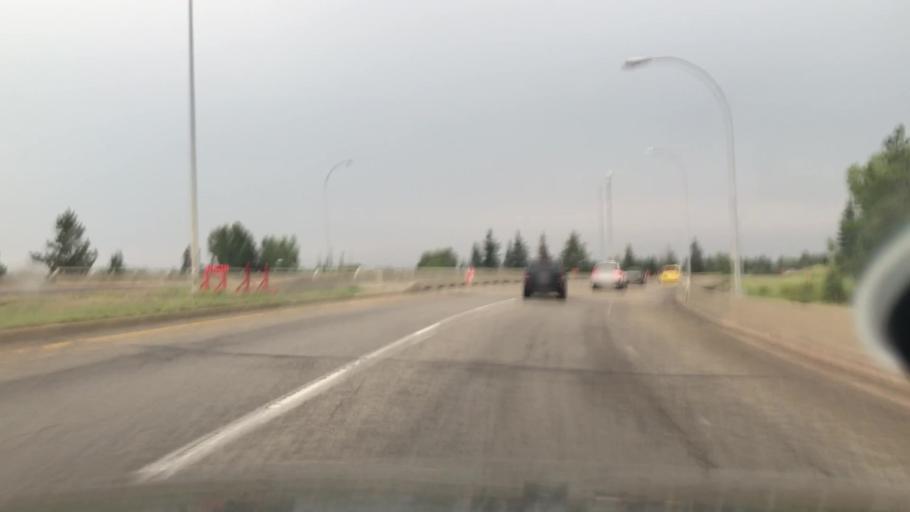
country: CA
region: Alberta
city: Edmonton
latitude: 53.4832
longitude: -113.5703
